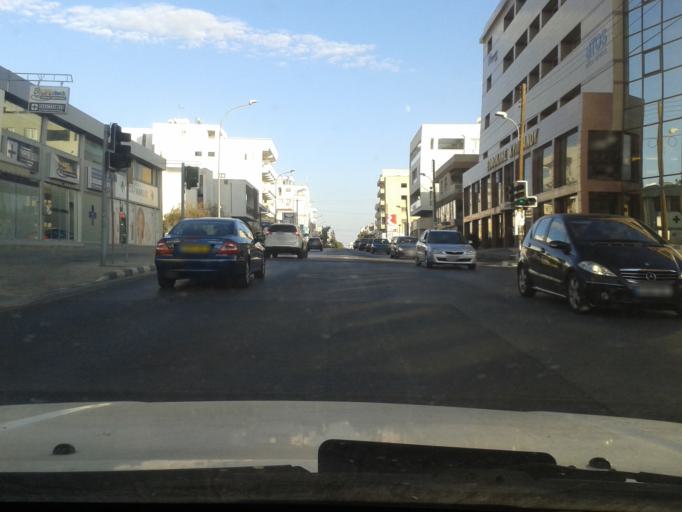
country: CY
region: Lefkosia
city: Nicosia
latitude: 35.1444
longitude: 33.3629
